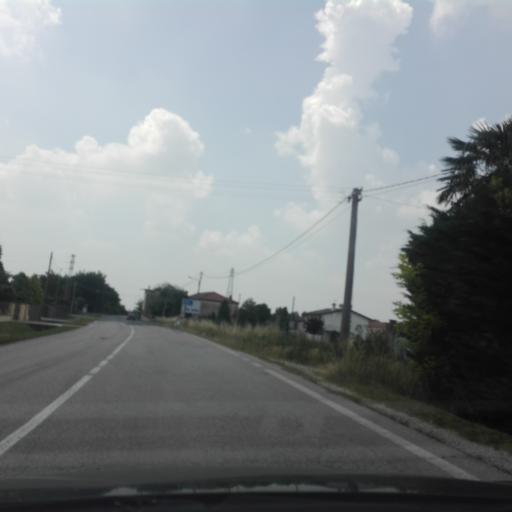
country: IT
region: Veneto
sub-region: Provincia di Rovigo
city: Villanova Marchesana
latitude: 44.9890
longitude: 11.9444
